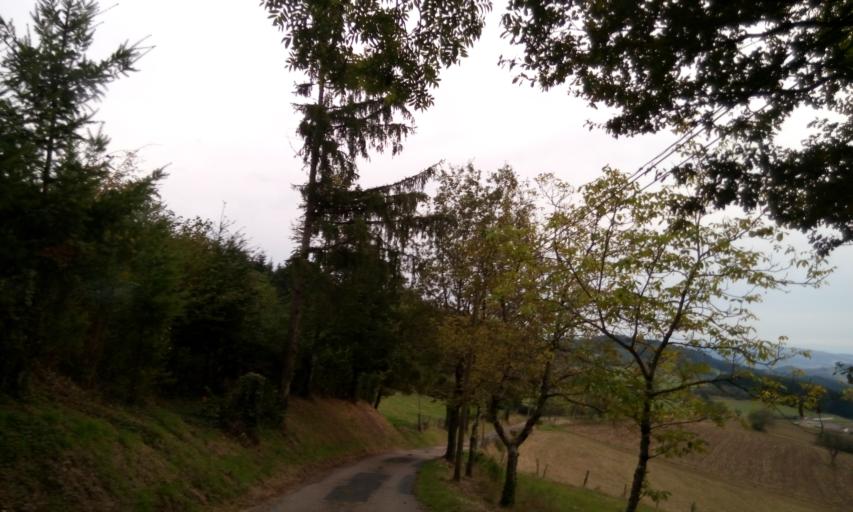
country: FR
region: Rhone-Alpes
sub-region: Departement du Rhone
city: Cours-la-Ville
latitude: 46.0778
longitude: 4.3694
